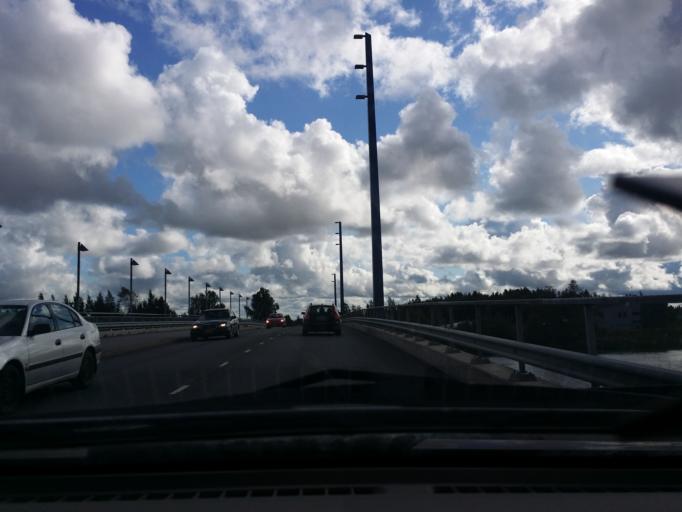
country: FI
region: Satakunta
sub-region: Pori
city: Pori
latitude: 61.4921
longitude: 21.8404
